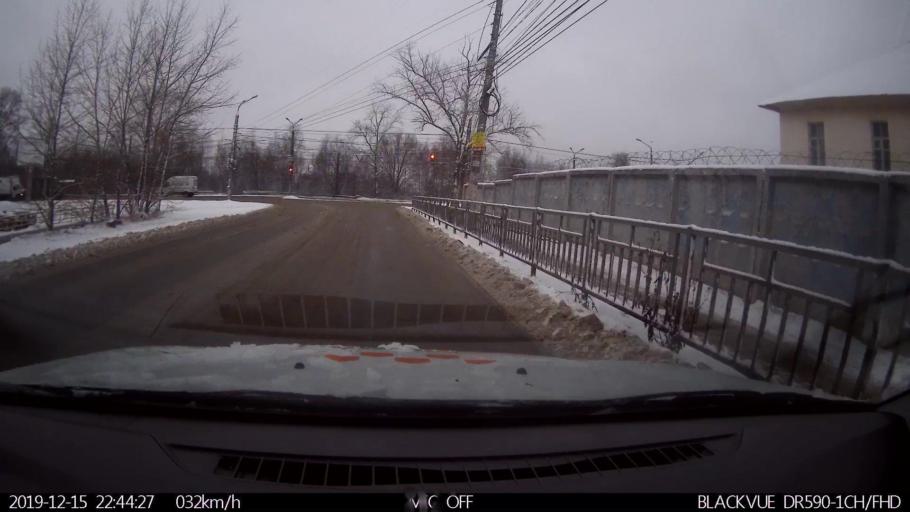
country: RU
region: Nizjnij Novgorod
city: Gorbatovka
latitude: 56.3114
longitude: 43.8411
